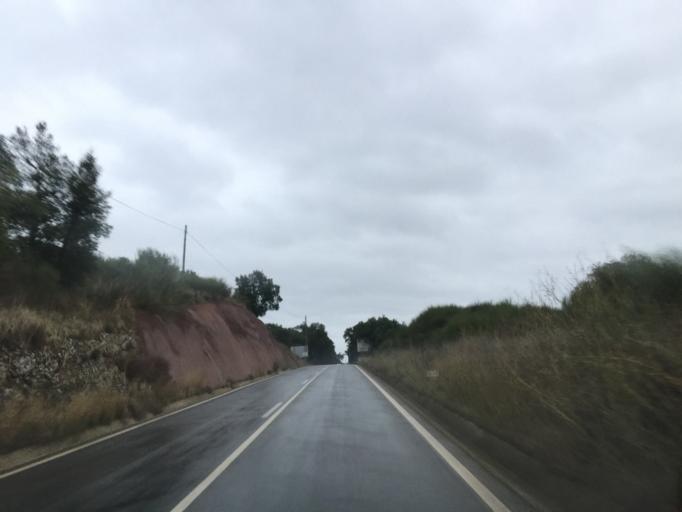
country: PT
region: Portalegre
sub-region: Avis
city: Avis
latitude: 39.0668
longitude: -7.8997
